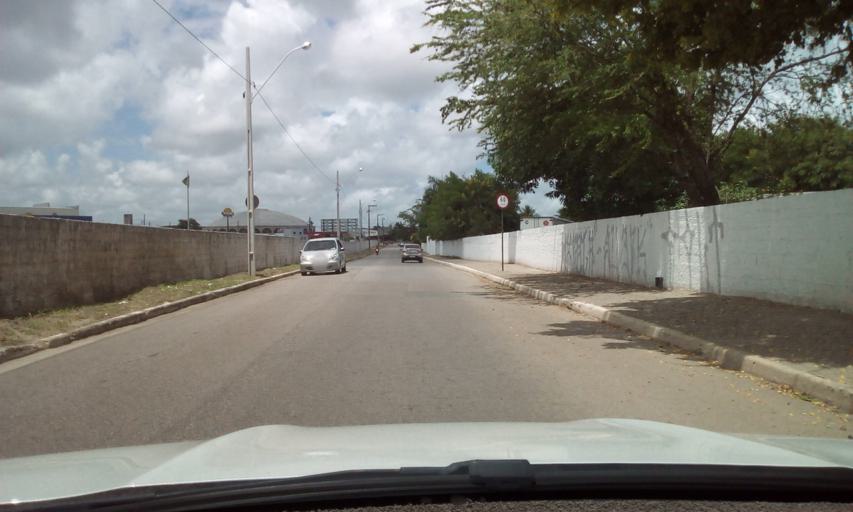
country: BR
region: Paraiba
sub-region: Joao Pessoa
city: Joao Pessoa
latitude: -7.1730
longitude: -34.8667
